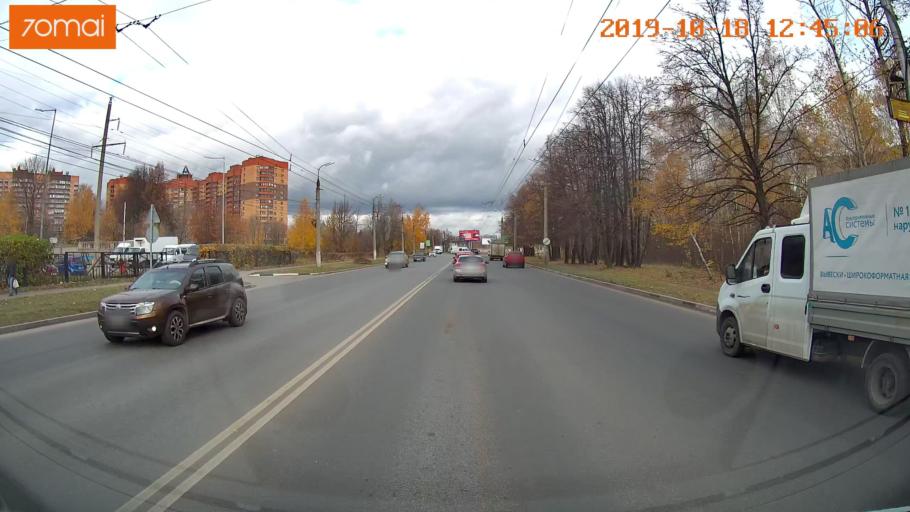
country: RU
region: Rjazan
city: Ryazan'
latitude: 54.6502
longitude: 39.6644
